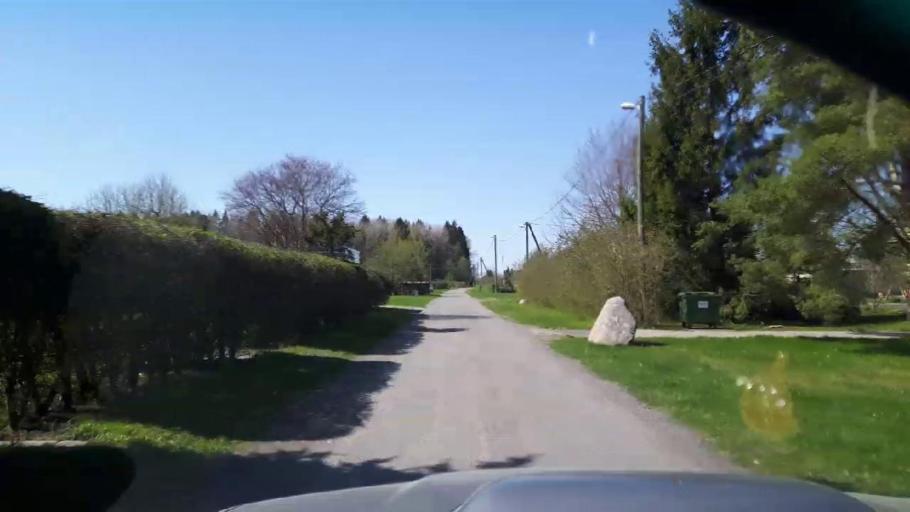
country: EE
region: Paernumaa
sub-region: Tootsi vald
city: Tootsi
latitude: 58.4748
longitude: 24.7937
